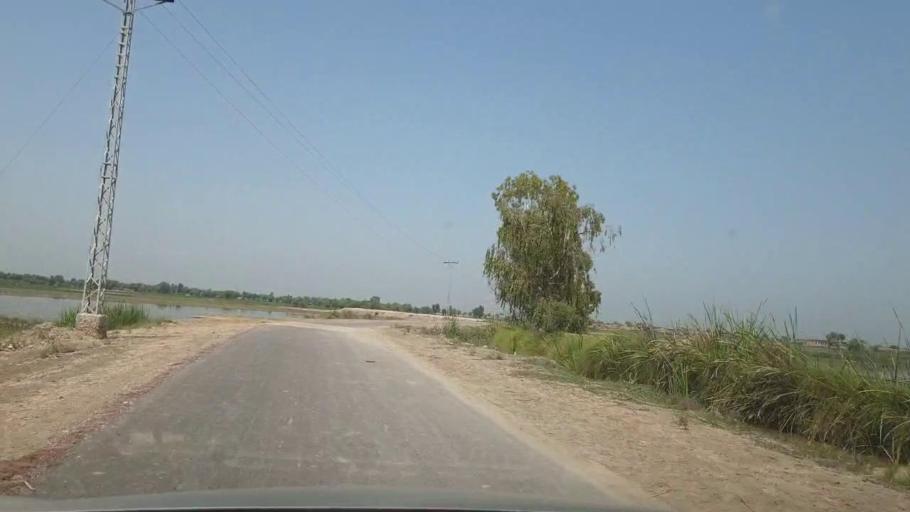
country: PK
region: Sindh
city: Warah
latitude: 27.4756
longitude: 67.7585
